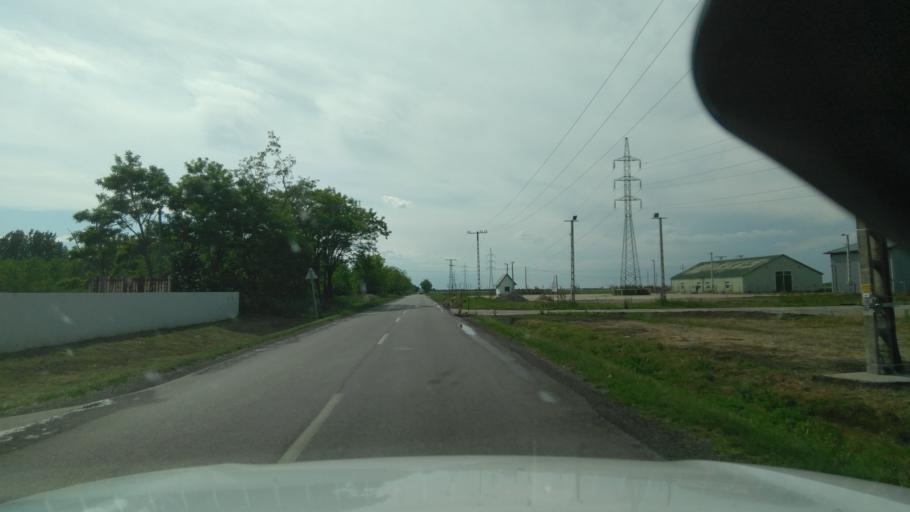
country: HU
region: Bekes
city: Medgyesegyhaza
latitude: 46.5057
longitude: 21.0099
